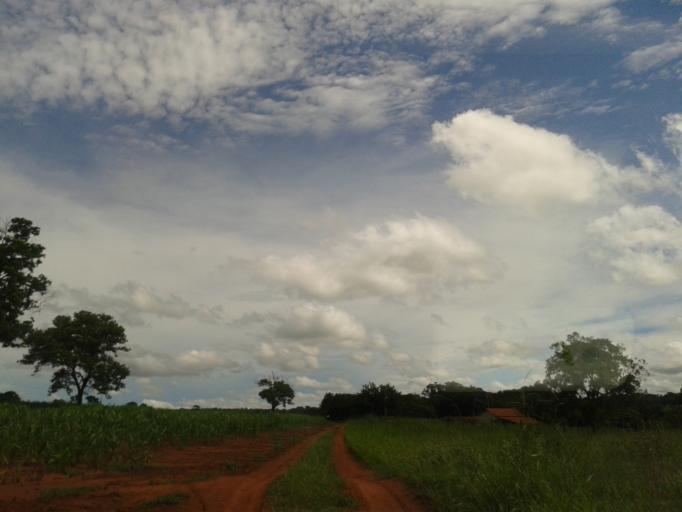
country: BR
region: Minas Gerais
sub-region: Santa Vitoria
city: Santa Vitoria
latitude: -19.1401
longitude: -50.4866
